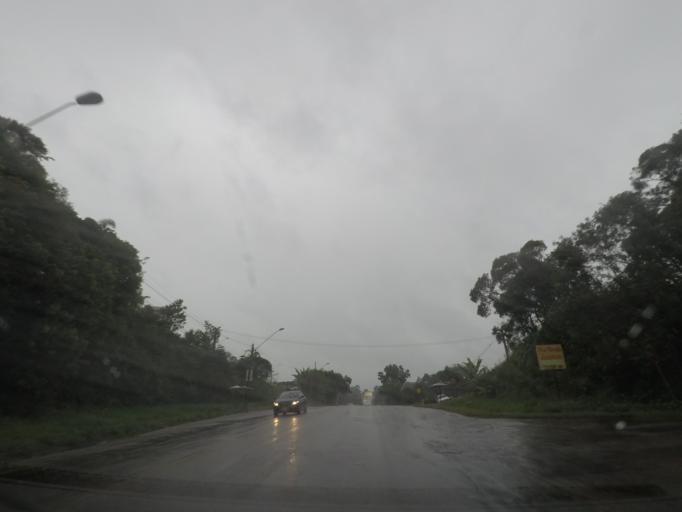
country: BR
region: Parana
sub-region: Almirante Tamandare
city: Almirante Tamandare
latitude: -25.3624
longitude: -49.2797
